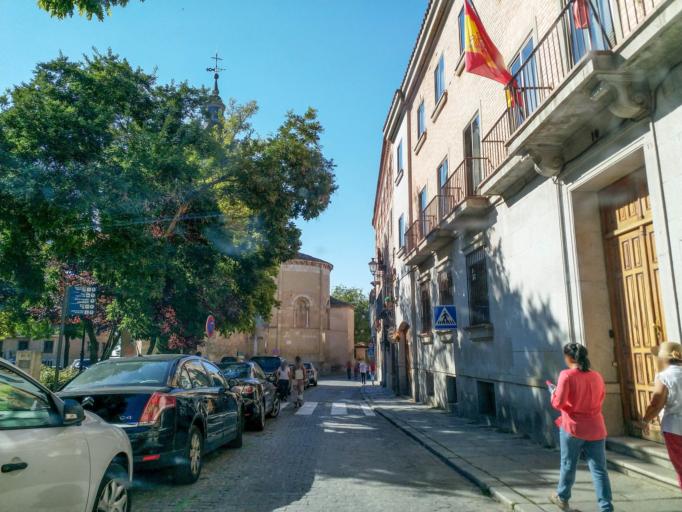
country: ES
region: Castille and Leon
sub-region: Provincia de Segovia
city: Segovia
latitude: 40.9514
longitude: -4.1271
